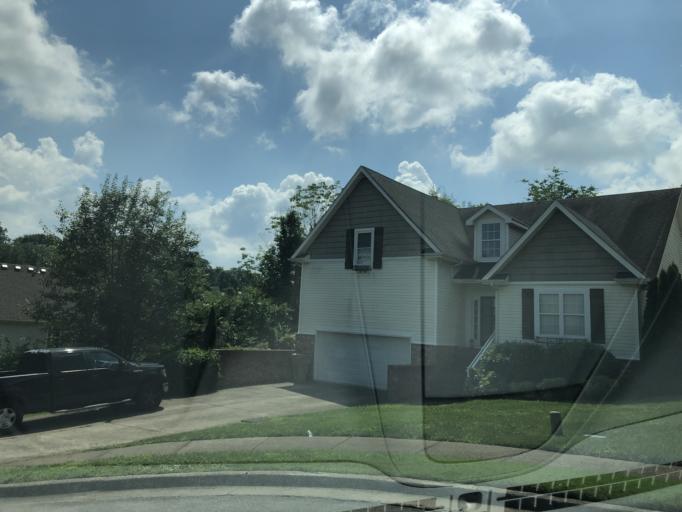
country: US
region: Tennessee
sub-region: Williamson County
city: Nolensville
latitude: 36.0169
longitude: -86.7026
